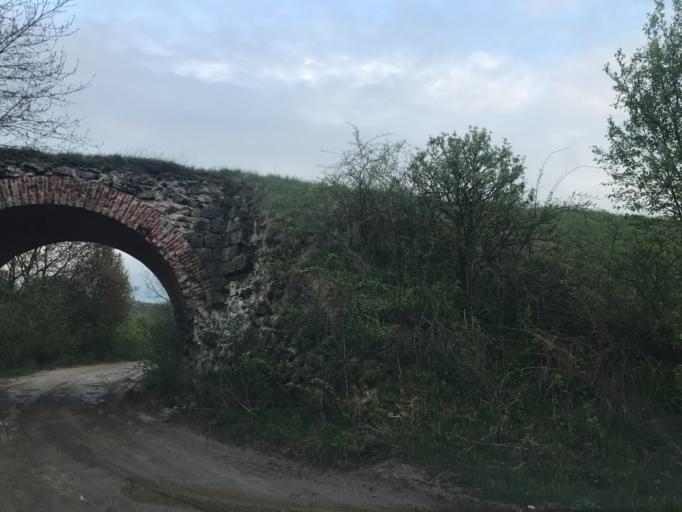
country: PL
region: Warmian-Masurian Voivodeship
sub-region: Powiat ilawski
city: Lubawa
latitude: 53.5343
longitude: 19.8938
